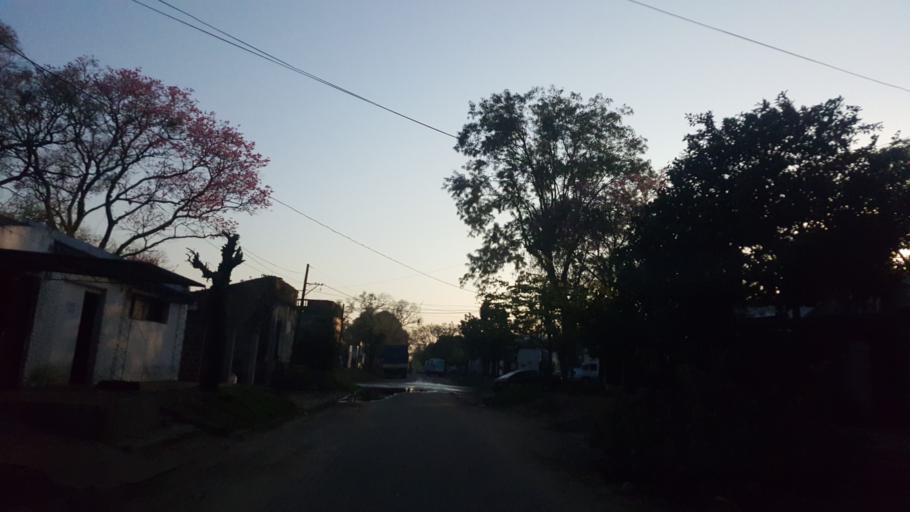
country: AR
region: Corrientes
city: Ituzaingo
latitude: -27.5882
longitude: -56.6868
